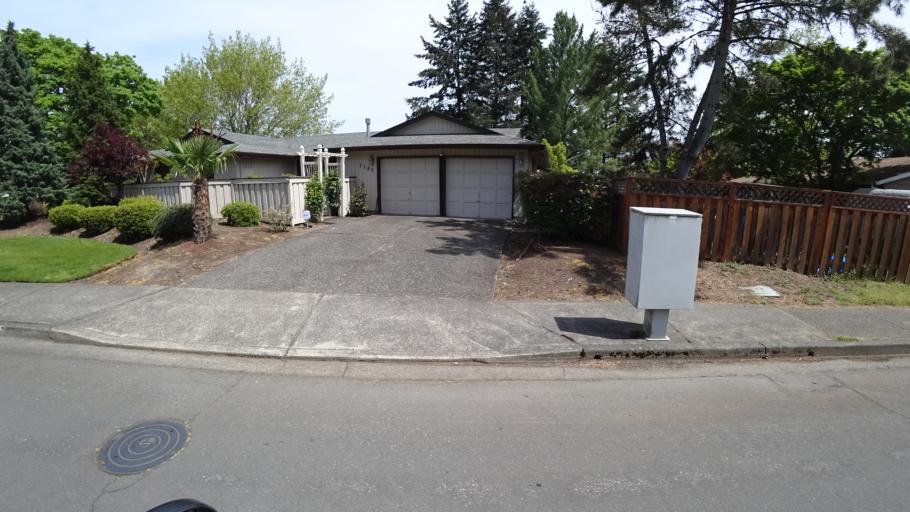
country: US
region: Oregon
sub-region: Washington County
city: Aloha
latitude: 45.4637
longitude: -122.8451
